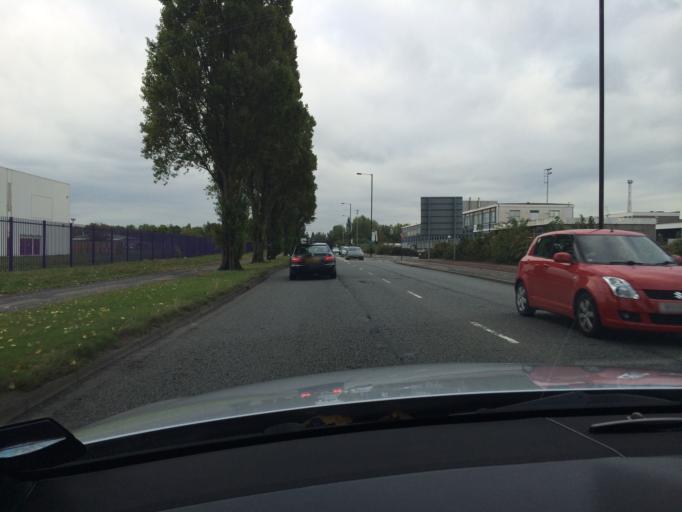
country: GB
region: England
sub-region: City and Borough of Salford
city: Eccles
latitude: 53.4647
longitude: -2.3398
